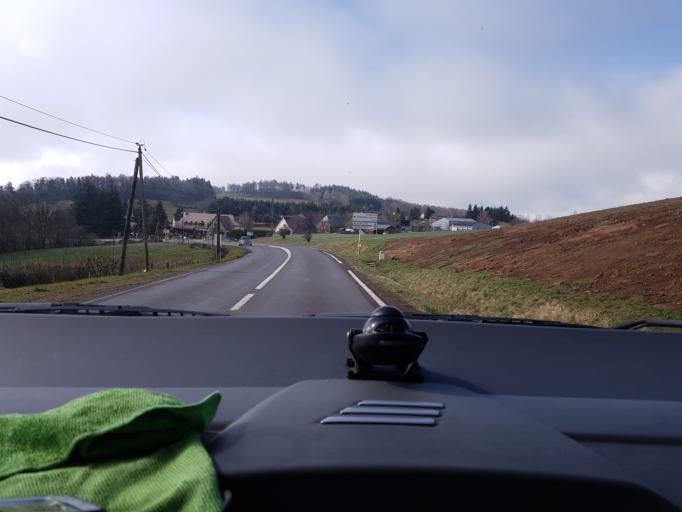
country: FR
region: Auvergne
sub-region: Departement du Cantal
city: Neuveglise
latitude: 44.9301
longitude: 2.9979
